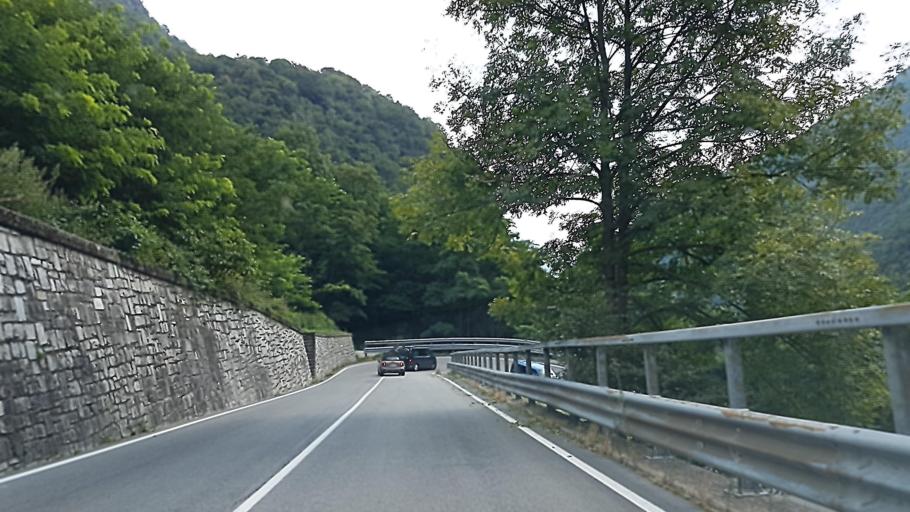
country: IT
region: Lombardy
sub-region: Provincia di Sondrio
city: San Giacomo Filippo
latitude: 46.3352
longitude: 9.3710
